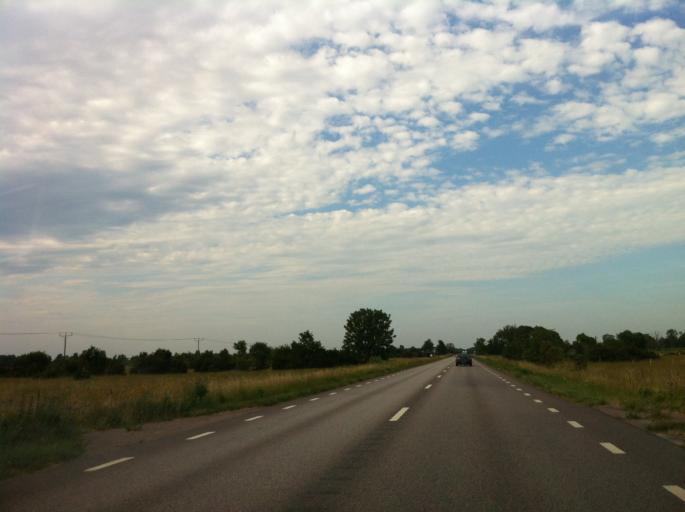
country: SE
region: Kalmar
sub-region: Borgholms Kommun
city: Borgholm
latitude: 56.9450
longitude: 16.7779
